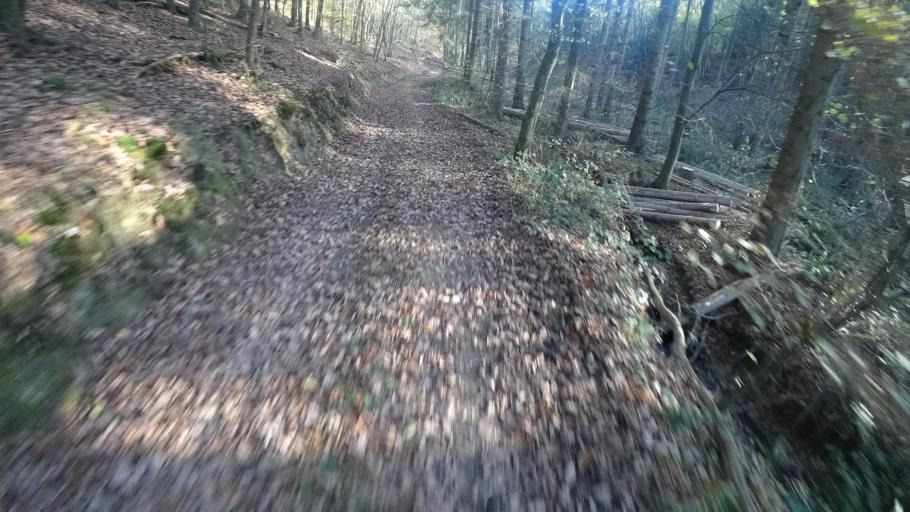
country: DE
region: Rheinland-Pfalz
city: Lind
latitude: 50.5113
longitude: 6.9468
